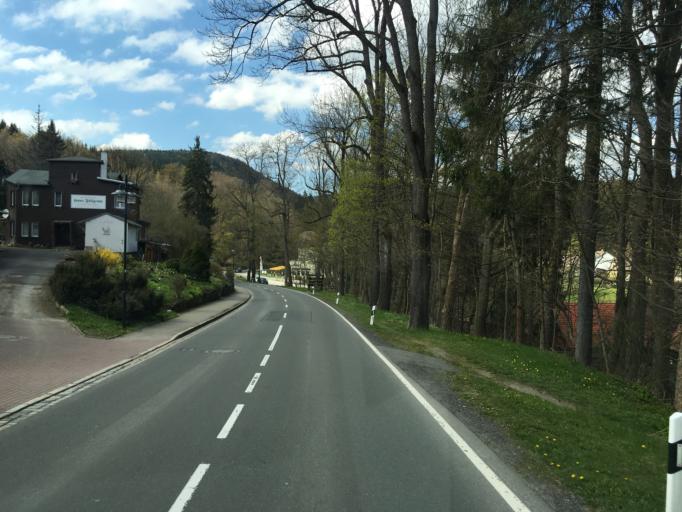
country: DE
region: Lower Saxony
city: Braunlage
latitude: 51.7421
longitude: 10.6837
